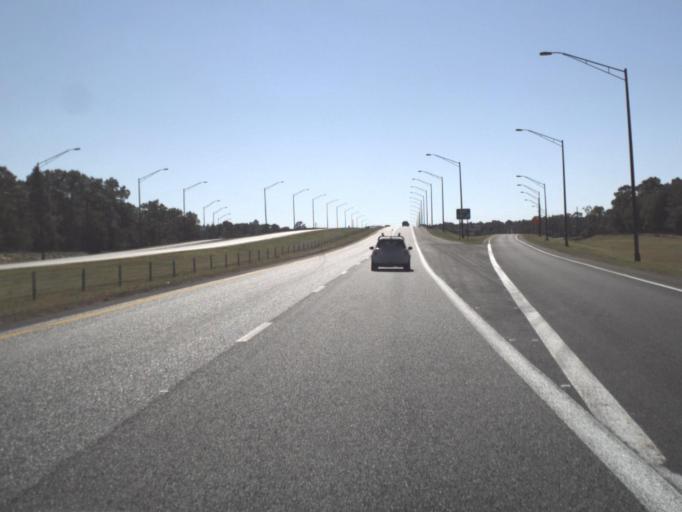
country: US
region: Florida
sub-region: Hernando County
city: Brookridge
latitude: 28.5389
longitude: -82.4796
